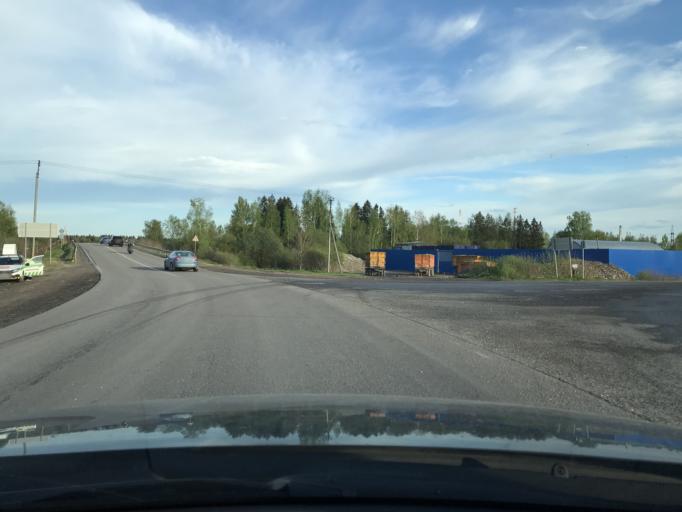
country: RU
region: Moskovskaya
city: Naro-Fominsk
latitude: 55.3528
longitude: 36.6919
